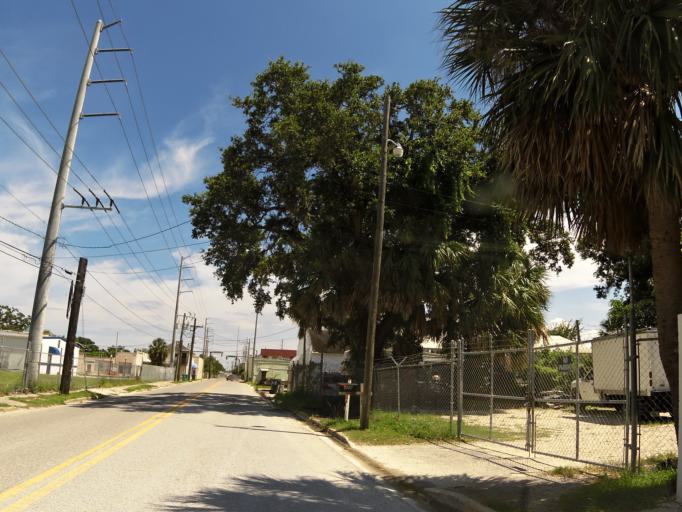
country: US
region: Florida
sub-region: Volusia County
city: Daytona Beach
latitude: 29.2157
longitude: -81.0275
